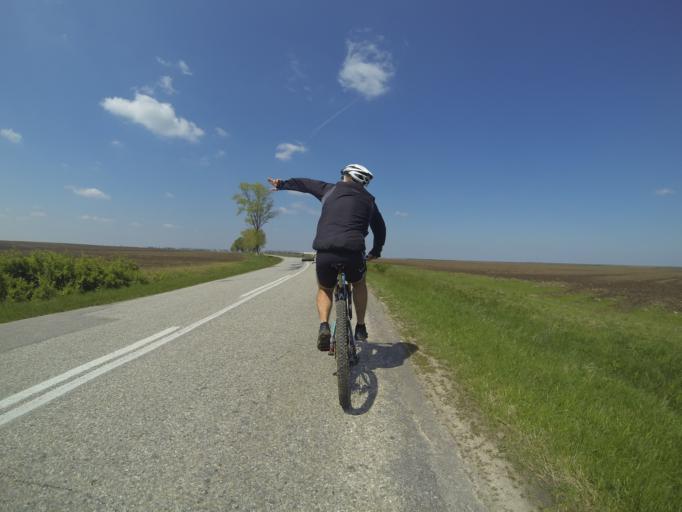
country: RO
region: Dolj
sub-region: Comuna Predesti
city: Predesti
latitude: 44.3011
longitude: 23.6041
